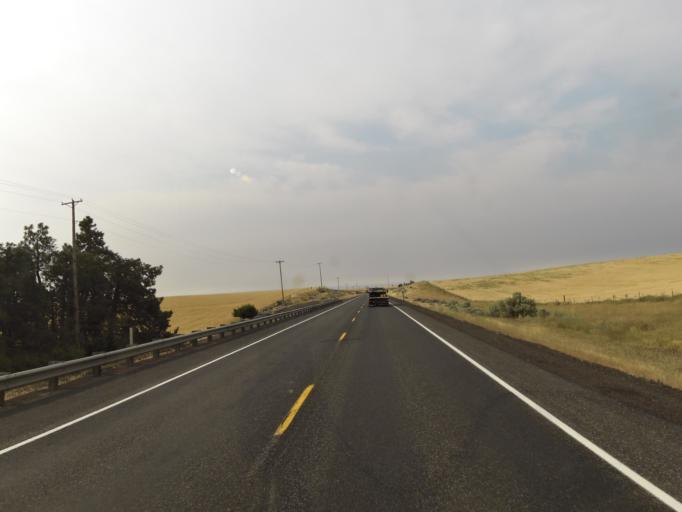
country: US
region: Oregon
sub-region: Sherman County
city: Moro
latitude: 45.3977
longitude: -120.7895
